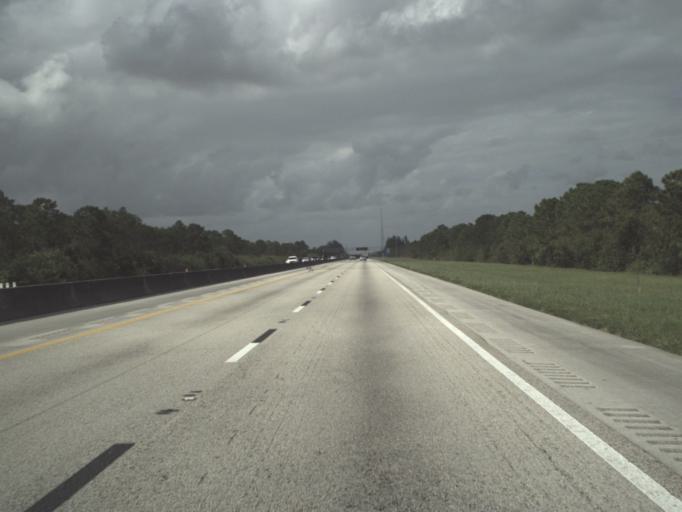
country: US
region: Florida
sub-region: Martin County
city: Palm City
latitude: 27.1389
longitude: -80.2893
